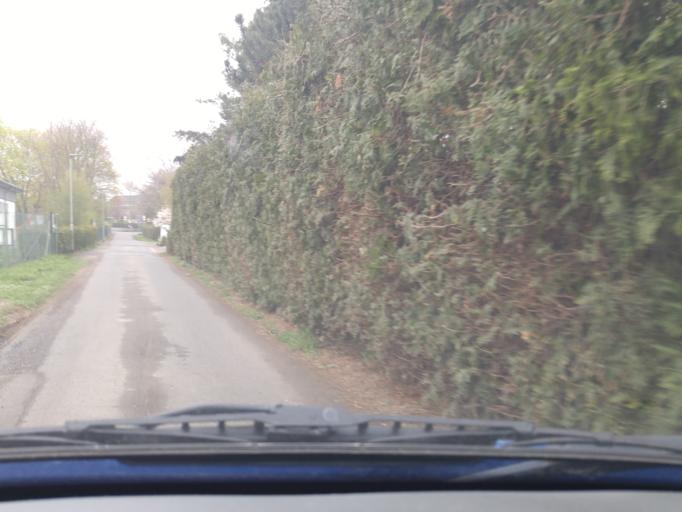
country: DE
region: Hesse
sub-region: Regierungsbezirk Darmstadt
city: Karben
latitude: 50.2813
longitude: 8.7772
